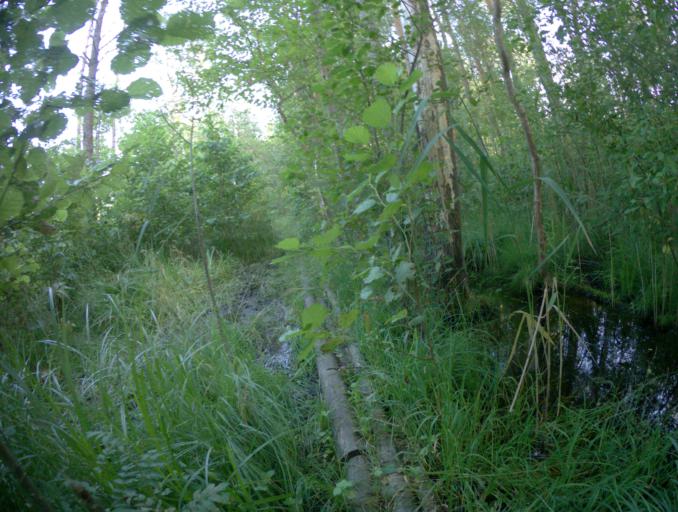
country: RU
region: Vladimir
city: Kommunar
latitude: 56.0929
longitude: 40.4611
